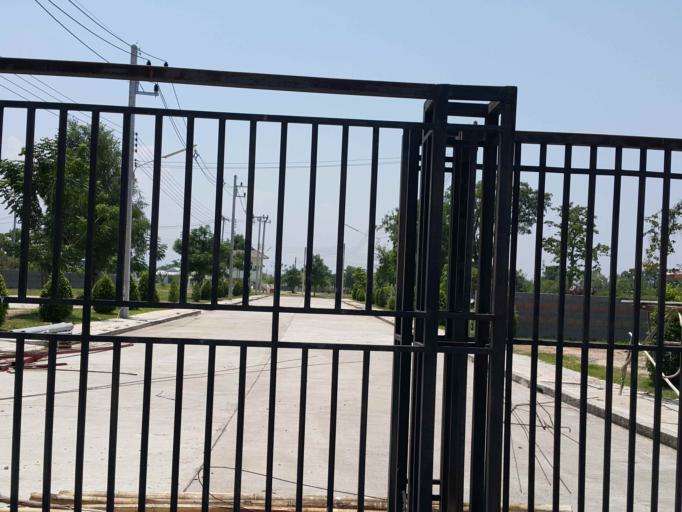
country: TH
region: Chiang Mai
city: San Sai
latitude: 18.8361
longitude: 99.1012
